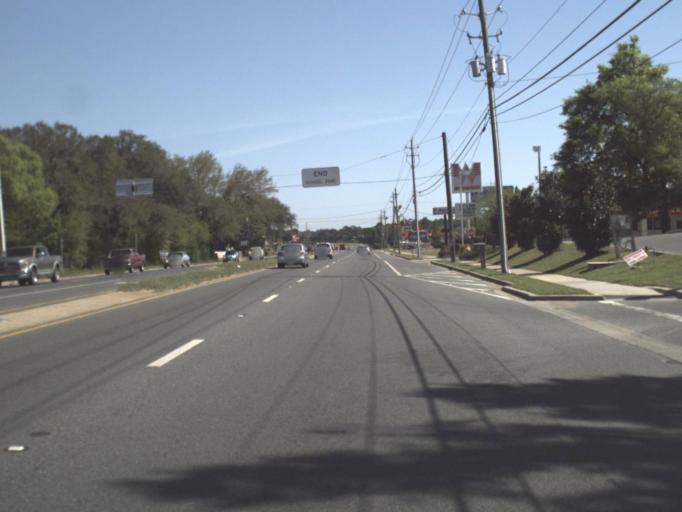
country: US
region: Florida
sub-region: Escambia County
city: Bellview
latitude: 30.4646
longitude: -87.3028
